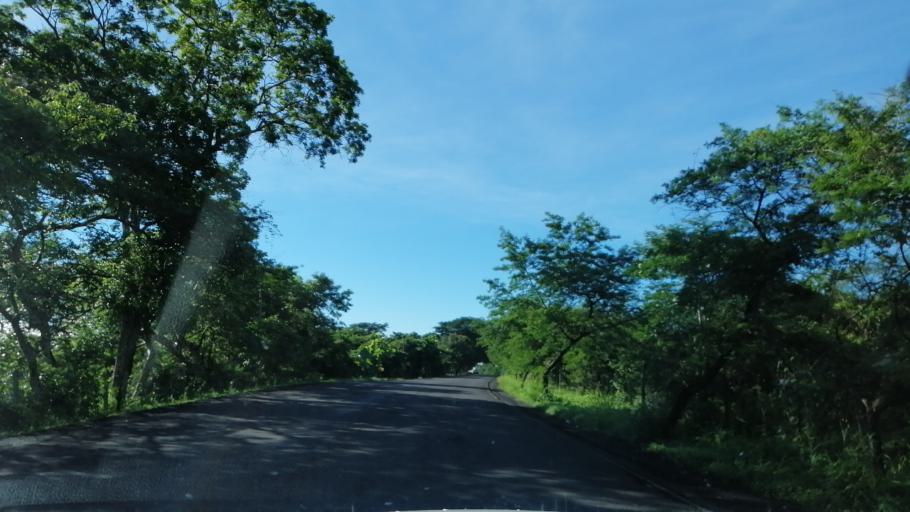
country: SV
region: Morazan
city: Cacaopera
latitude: 13.7841
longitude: -88.1059
